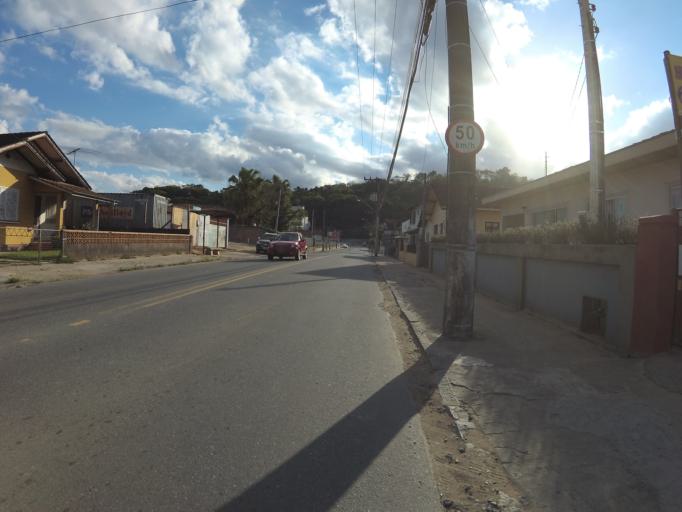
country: BR
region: Santa Catarina
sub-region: Blumenau
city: Blumenau
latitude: -26.8762
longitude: -49.0999
